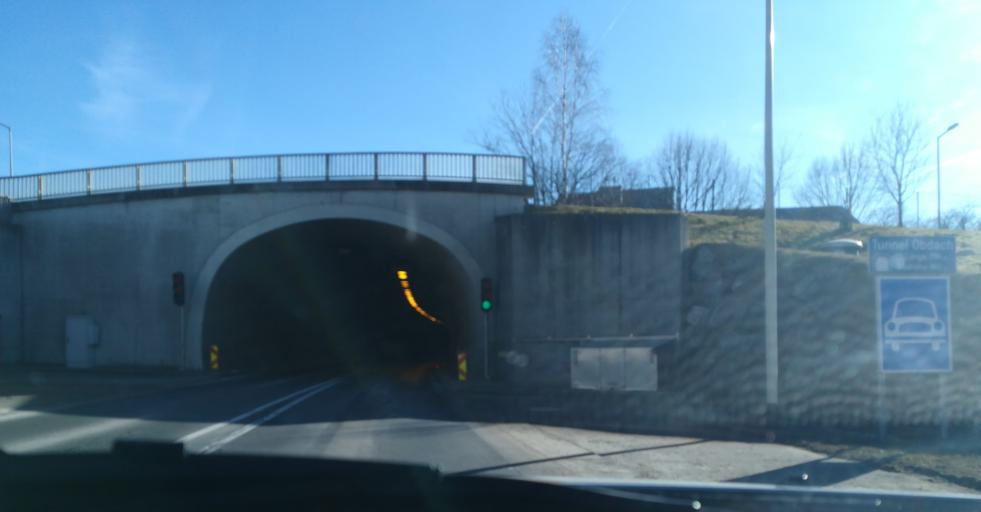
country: AT
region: Styria
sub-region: Politischer Bezirk Murtal
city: Obdach
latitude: 47.0711
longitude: 14.6960
